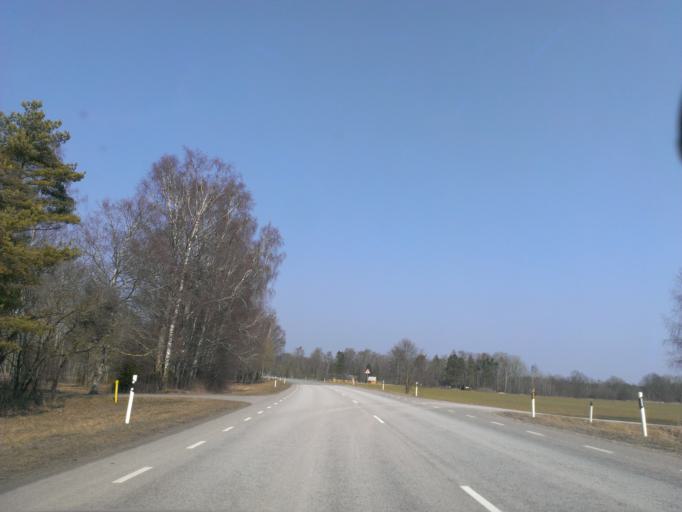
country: EE
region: Saare
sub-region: Orissaare vald
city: Orissaare
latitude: 58.4810
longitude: 22.8358
